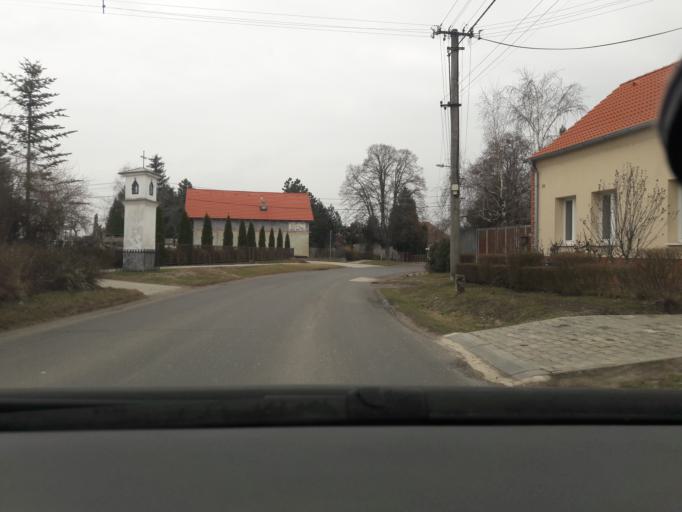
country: SK
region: Bratislavsky
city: Senec
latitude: 48.2968
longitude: 17.4536
